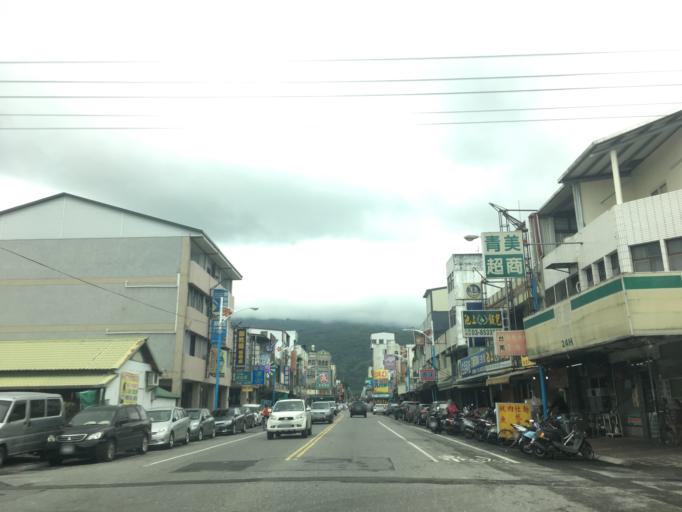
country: TW
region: Taiwan
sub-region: Hualien
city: Hualian
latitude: 23.9790
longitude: 121.5685
